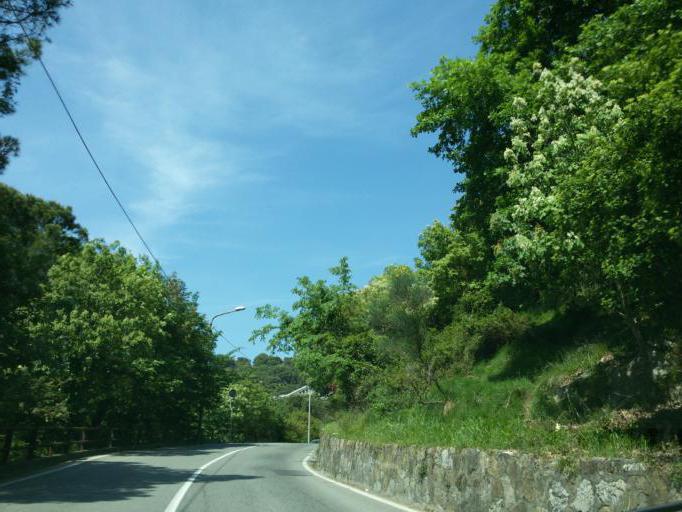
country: IT
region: Liguria
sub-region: Provincia di Genova
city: Genoa
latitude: 44.4223
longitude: 8.9611
